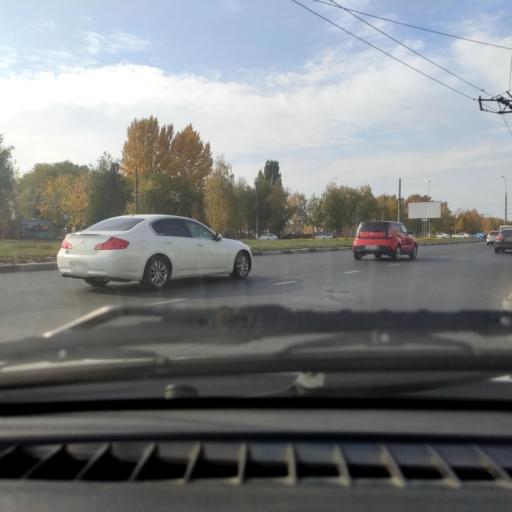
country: RU
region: Samara
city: Tol'yatti
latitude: 53.4986
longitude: 49.2887
